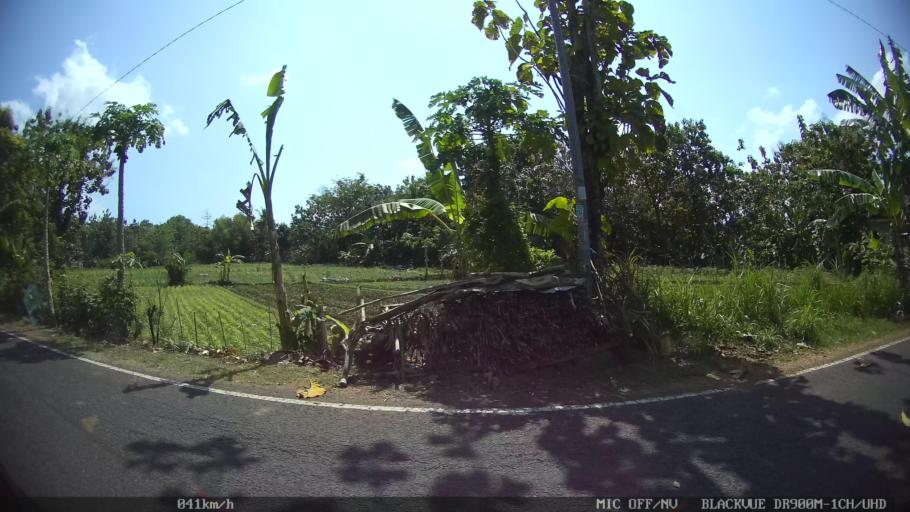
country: ID
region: Daerah Istimewa Yogyakarta
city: Pundong
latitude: -7.9573
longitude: 110.3640
